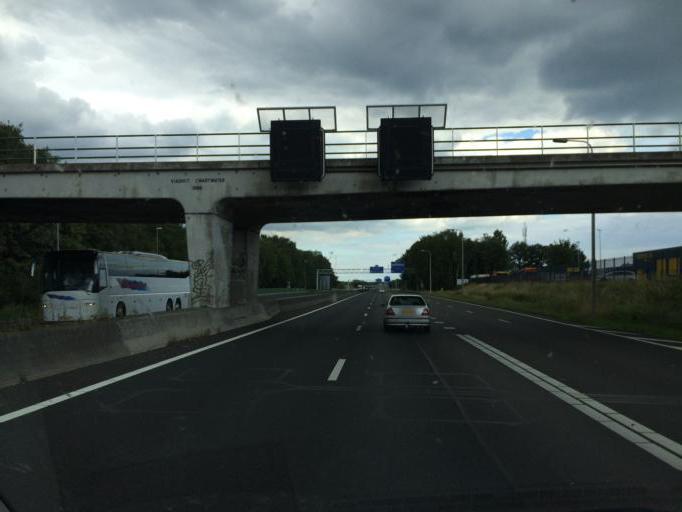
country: NL
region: Limburg
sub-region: Gemeente Venlo
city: Venlo
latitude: 51.3933
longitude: 6.1859
